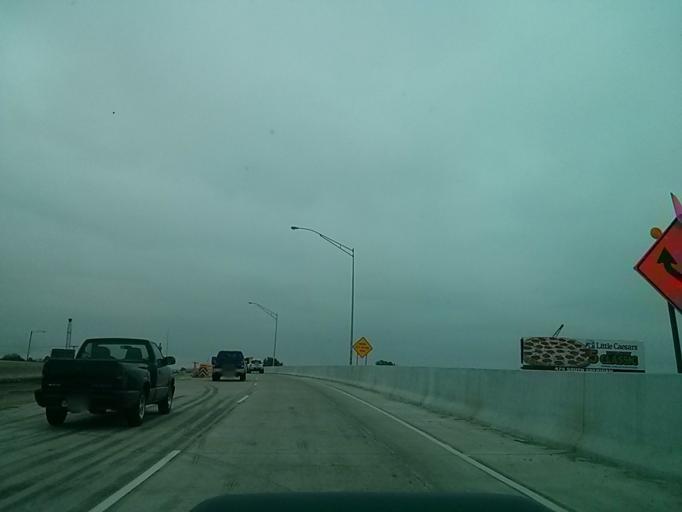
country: US
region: Oklahoma
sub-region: Tulsa County
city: Tulsa
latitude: 36.1592
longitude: -95.9166
